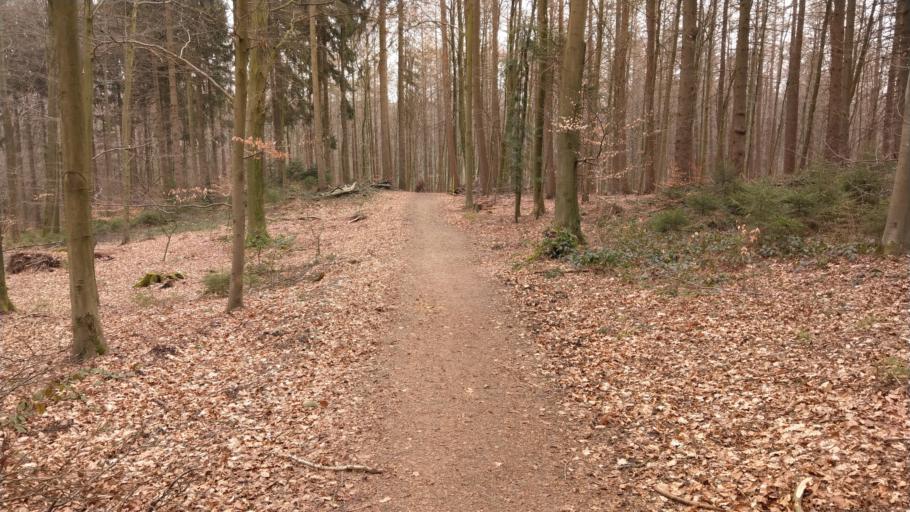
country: NL
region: Limburg
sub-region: Gemeente Vaals
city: Vaals
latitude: 50.7445
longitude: 6.0479
